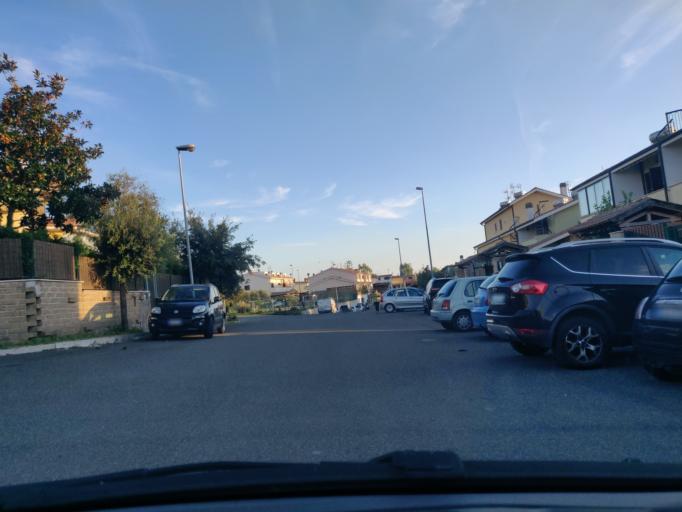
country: IT
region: Latium
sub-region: Citta metropolitana di Roma Capitale
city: Civitavecchia
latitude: 42.0641
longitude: 11.8179
